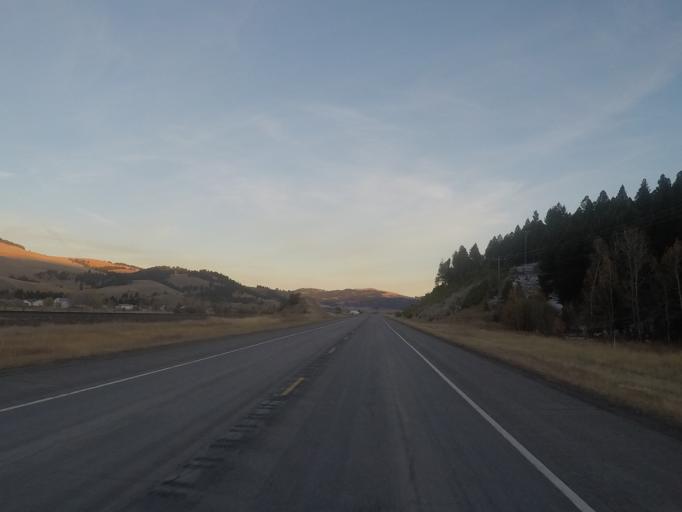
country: US
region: Montana
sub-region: Powell County
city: Deer Lodge
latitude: 46.5656
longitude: -112.4505
